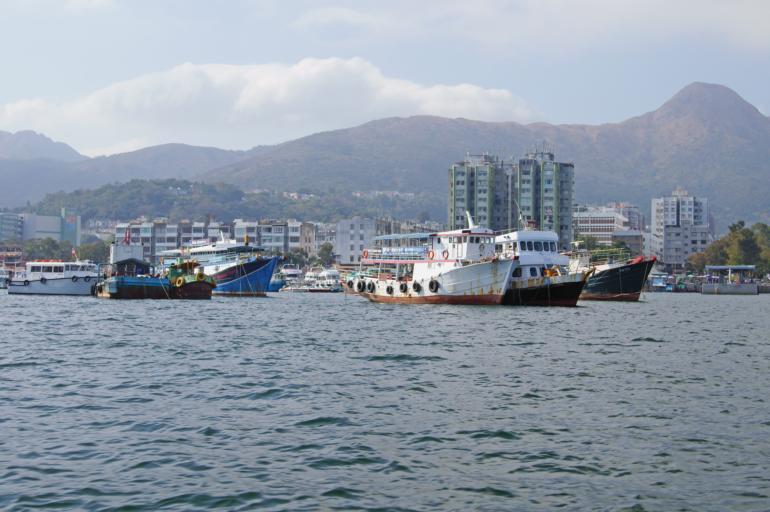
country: HK
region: Sai Kung
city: Sai Kung
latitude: 22.3795
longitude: 114.2770
